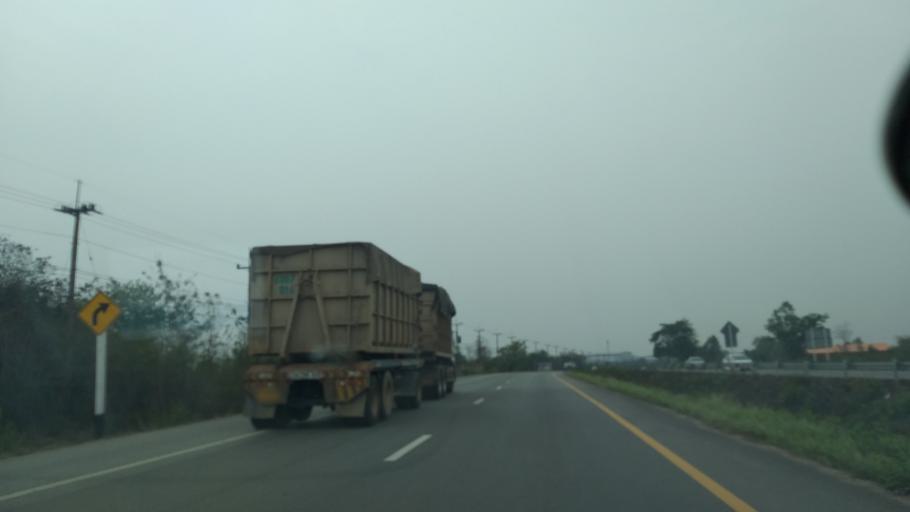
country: TH
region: Chachoengsao
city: Plaeng Yao
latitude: 13.4938
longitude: 101.2739
